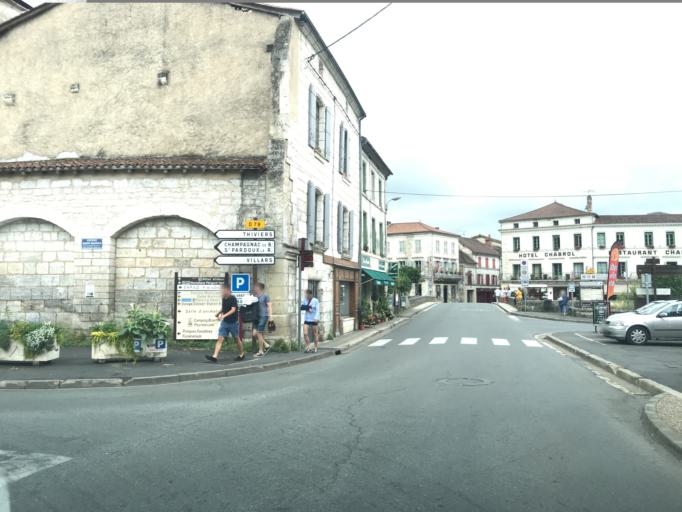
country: FR
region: Aquitaine
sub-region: Departement de la Dordogne
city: Brantome
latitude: 45.3659
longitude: 0.6503
